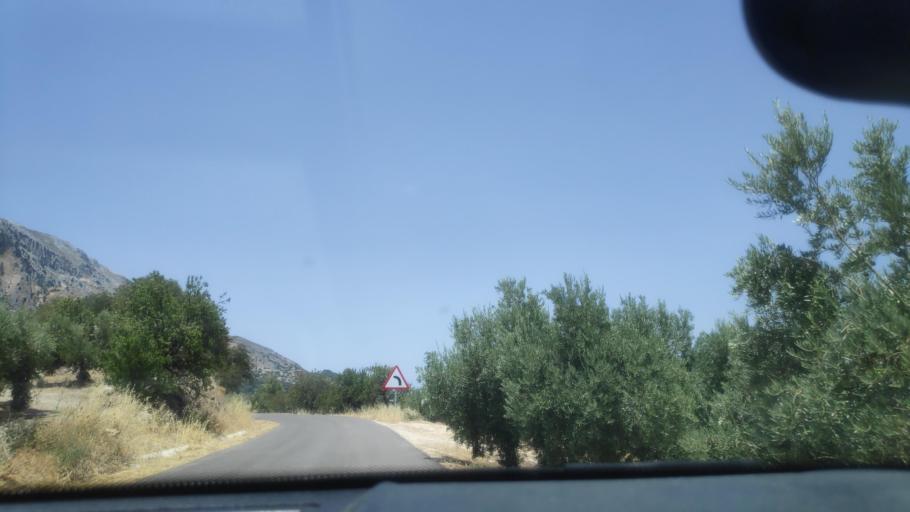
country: ES
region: Andalusia
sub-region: Provincia de Jaen
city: Jimena
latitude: 37.7998
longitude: -3.4486
